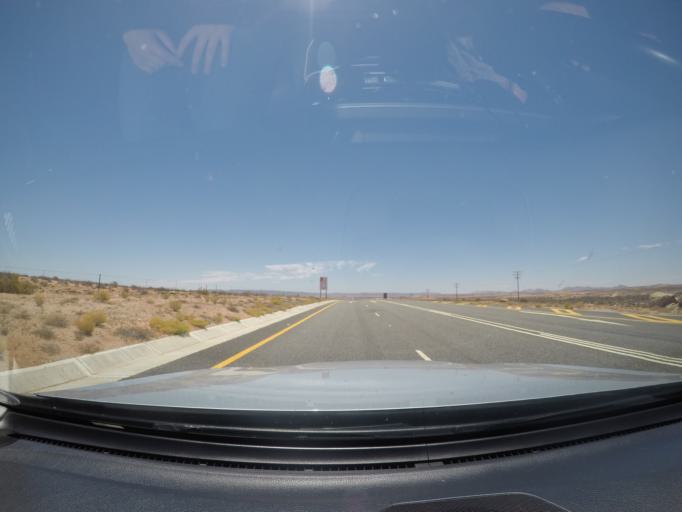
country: ZA
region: Northern Cape
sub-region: Namakwa District Municipality
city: Springbok
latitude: -29.3818
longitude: 17.7993
